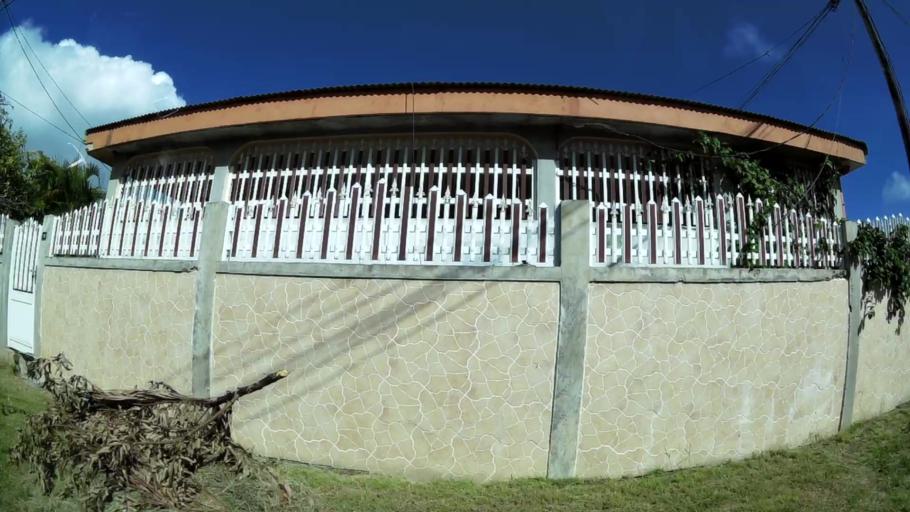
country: GP
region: Guadeloupe
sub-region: Guadeloupe
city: Sainte-Anne
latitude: 16.2301
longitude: -61.3766
